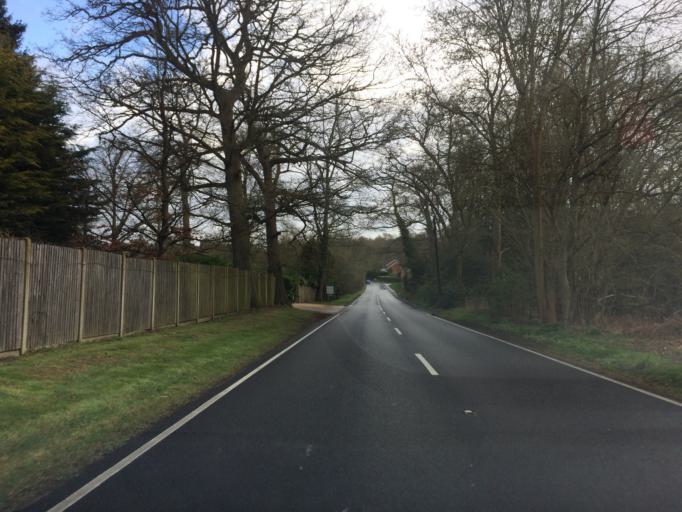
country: GB
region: England
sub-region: Surrey
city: Ottershaw
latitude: 51.3574
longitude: -0.5524
